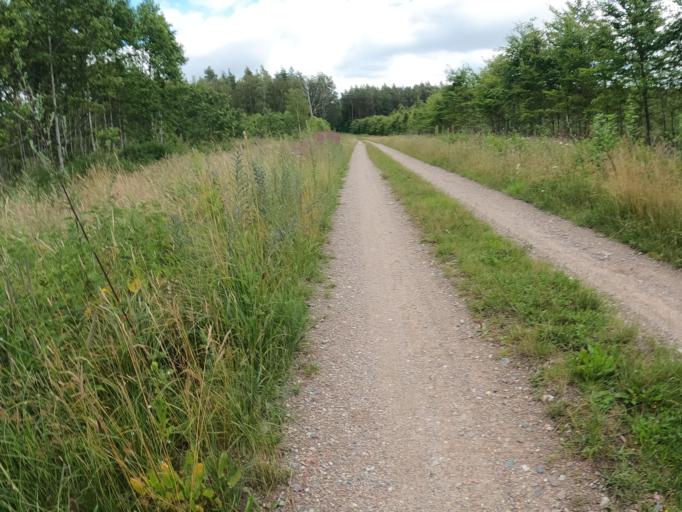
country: PL
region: West Pomeranian Voivodeship
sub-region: Powiat bialogardzki
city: Karlino
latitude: 53.9964
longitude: 15.9160
